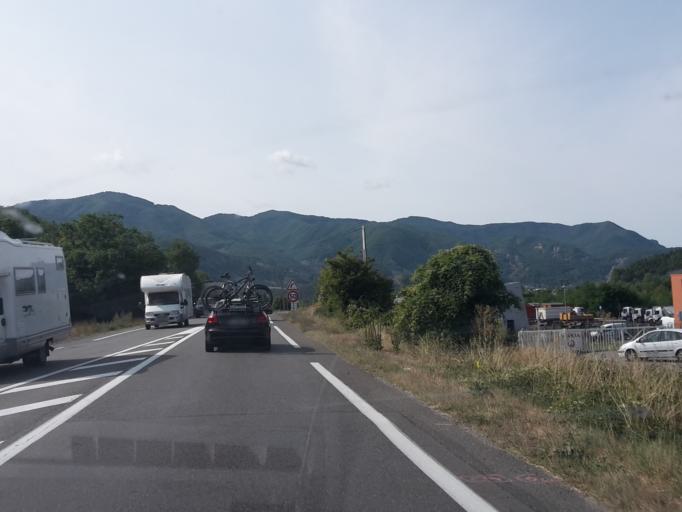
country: FR
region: Provence-Alpes-Cote d'Azur
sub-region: Departement des Hautes-Alpes
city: Tallard
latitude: 44.4456
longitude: 6.0319
